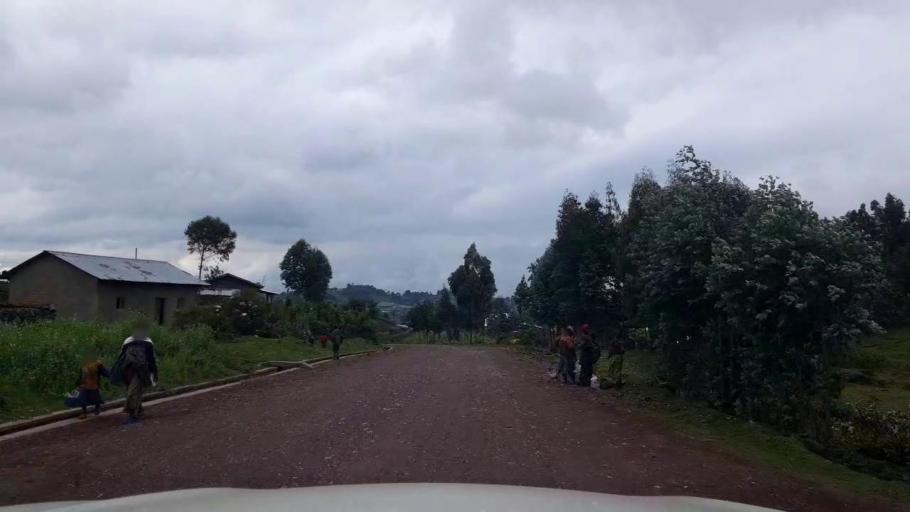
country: RW
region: Northern Province
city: Musanze
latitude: -1.5913
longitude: 29.4618
